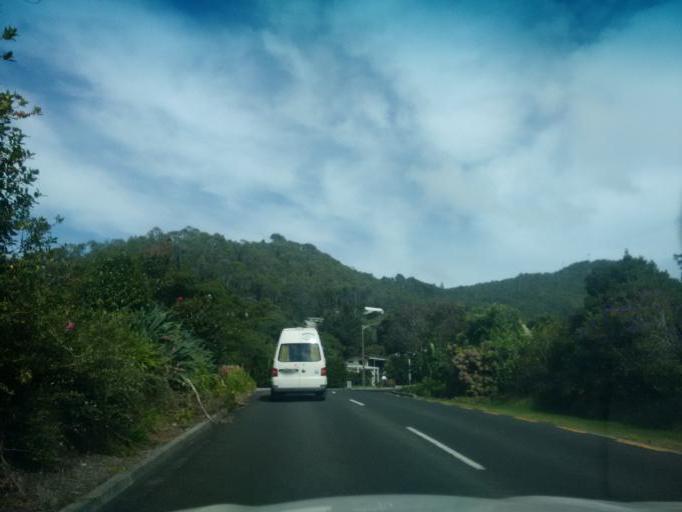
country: NZ
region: Waikato
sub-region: Thames-Coromandel District
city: Whitianga
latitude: -36.8397
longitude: 175.8011
